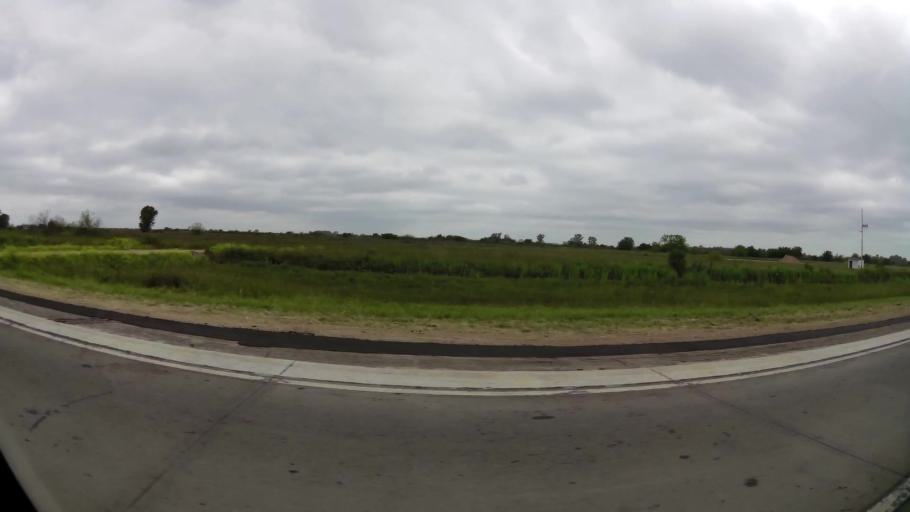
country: AR
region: Buenos Aires
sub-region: Partido de San Vicente
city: San Vicente
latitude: -35.0313
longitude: -58.3861
